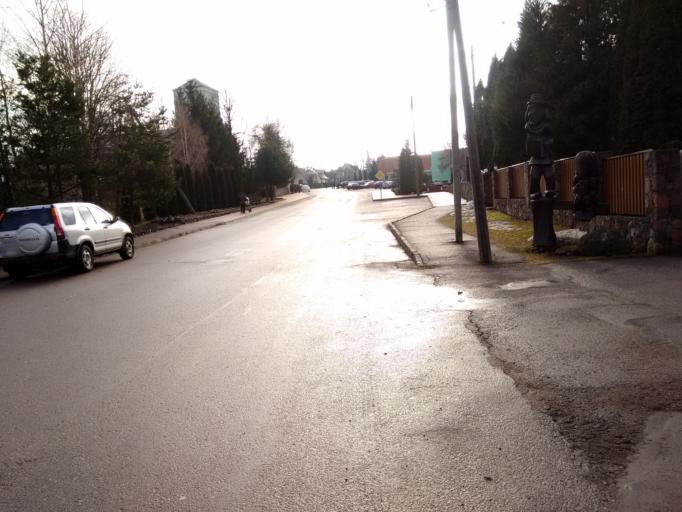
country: LT
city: Veisiejai
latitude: 54.2313
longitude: 23.8139
